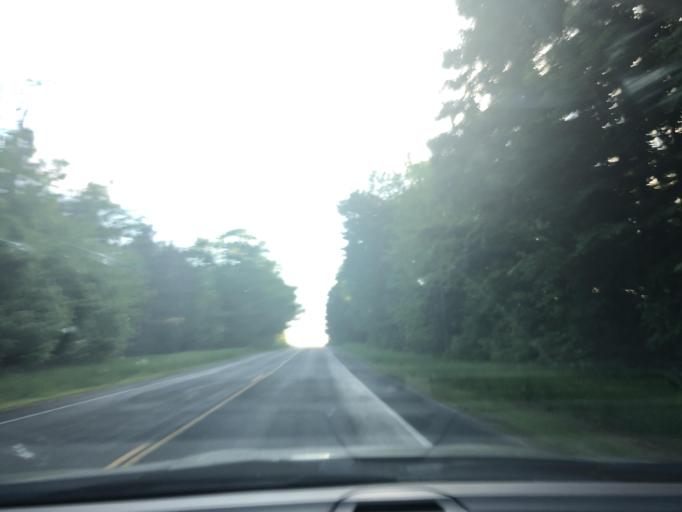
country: US
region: Michigan
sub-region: Missaukee County
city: Lake City
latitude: 44.4669
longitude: -85.1059
